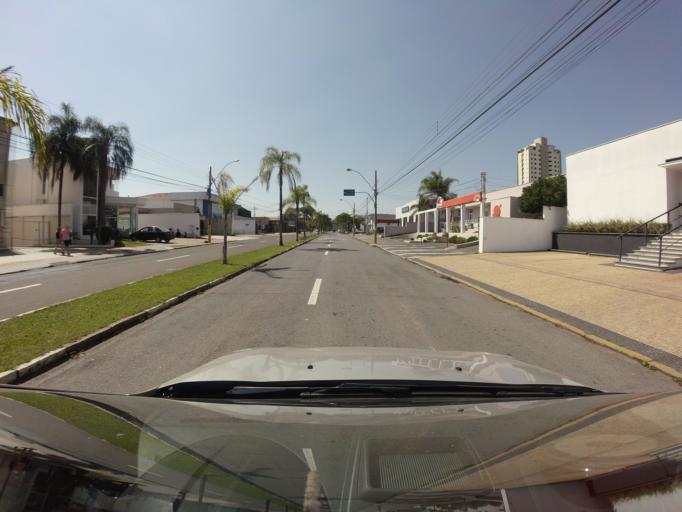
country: BR
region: Sao Paulo
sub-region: Piracicaba
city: Piracicaba
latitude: -22.7146
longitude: -47.6375
